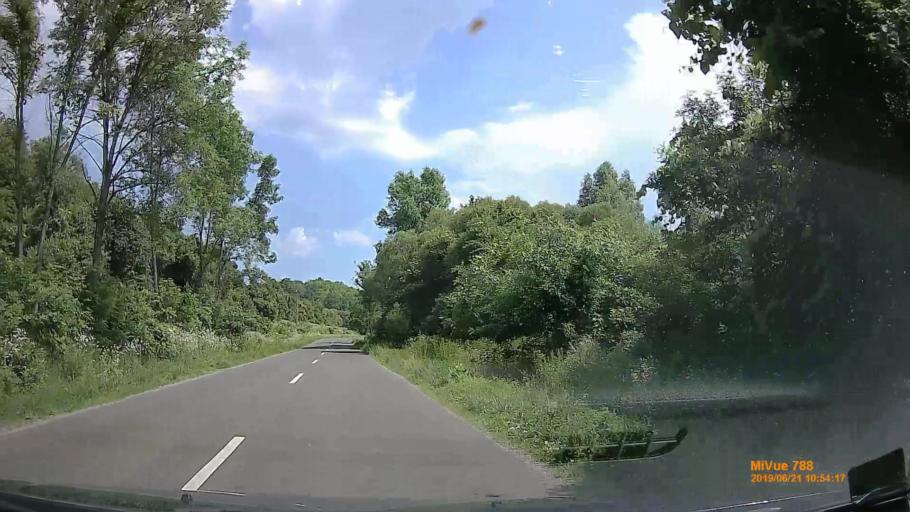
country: HU
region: Baranya
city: Buekkoesd
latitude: 46.1518
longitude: 18.0644
